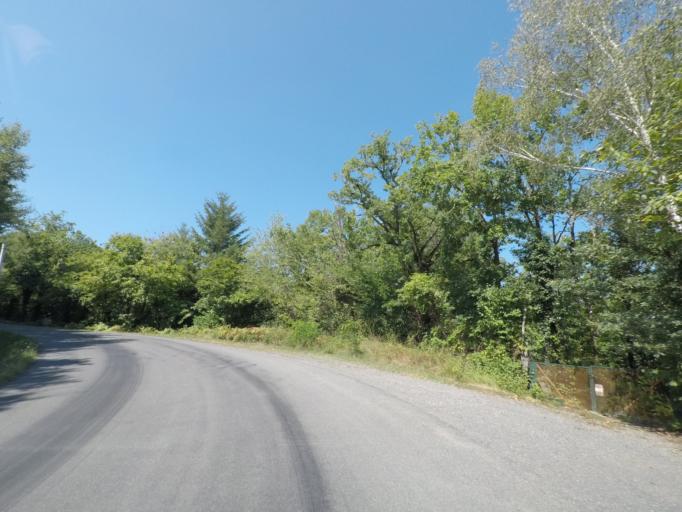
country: FR
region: Midi-Pyrenees
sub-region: Departement de l'Aveyron
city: Livinhac-le-Haut
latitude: 44.6103
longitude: 2.2263
